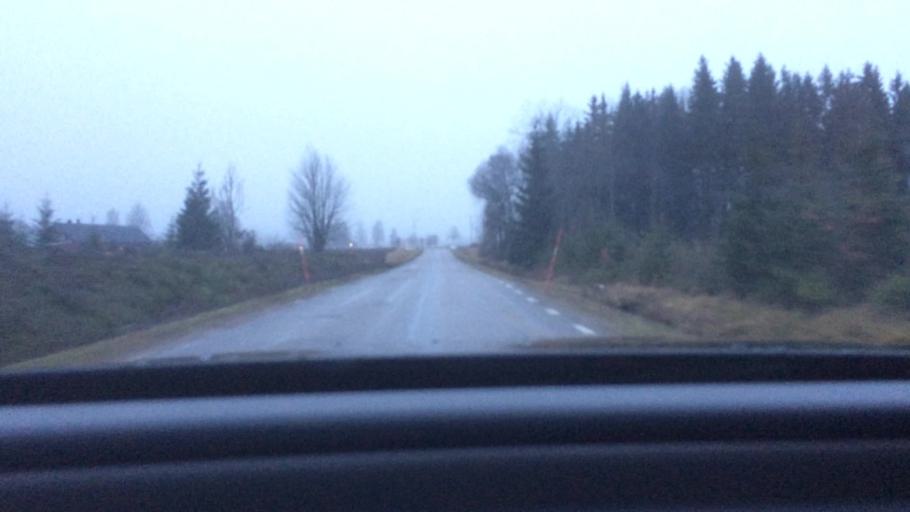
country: SE
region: Vaestra Goetaland
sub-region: Ulricehamns Kommun
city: Ulricehamn
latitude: 57.9469
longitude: 13.3858
